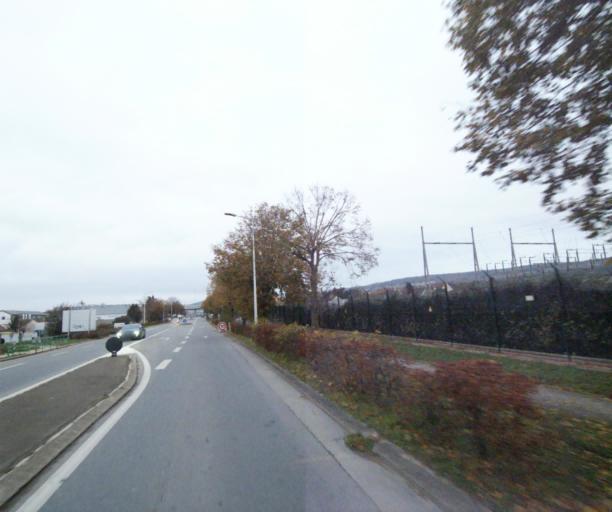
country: FR
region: Ile-de-France
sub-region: Departement des Yvelines
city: Triel-sur-Seine
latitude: 48.9663
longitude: 2.0122
